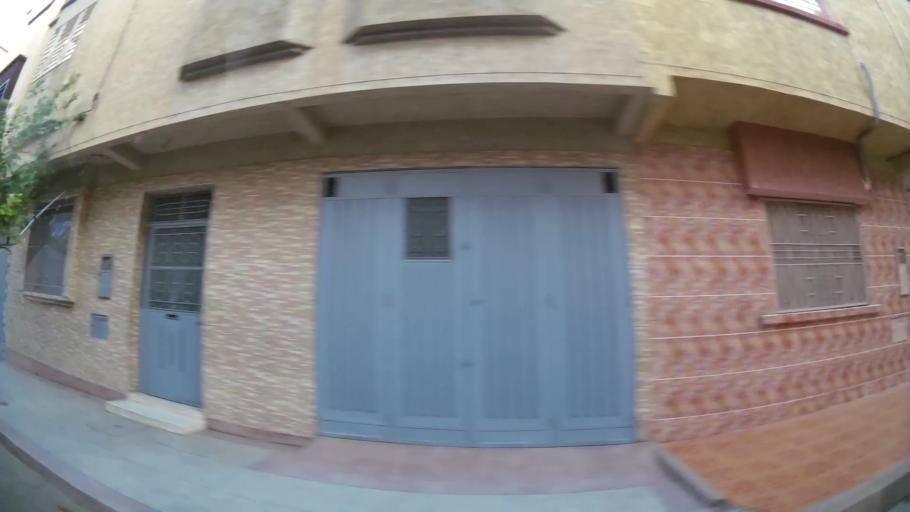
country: MA
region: Oriental
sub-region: Oujda-Angad
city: Oujda
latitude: 34.7057
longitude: -1.9122
